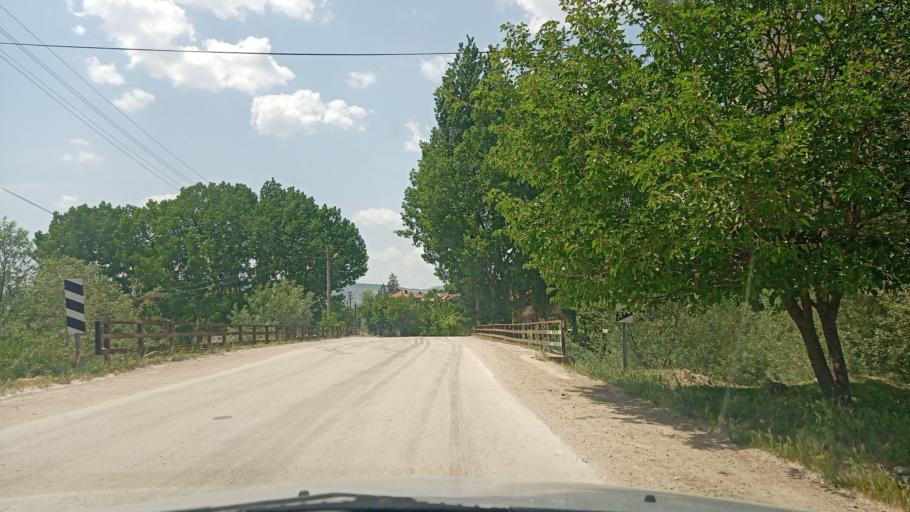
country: TR
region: Bolu
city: Seben
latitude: 40.4073
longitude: 31.5800
